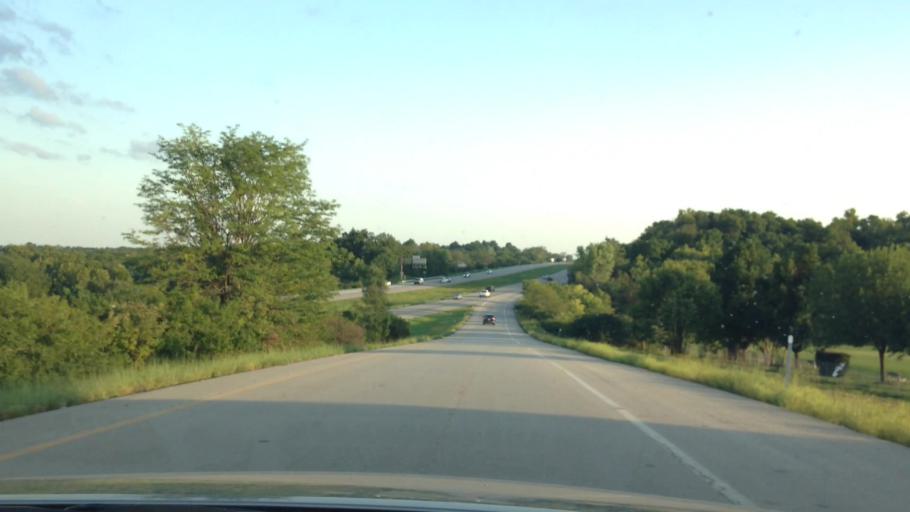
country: US
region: Missouri
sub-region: Clay County
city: Pleasant Valley
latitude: 39.2668
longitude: -94.5113
